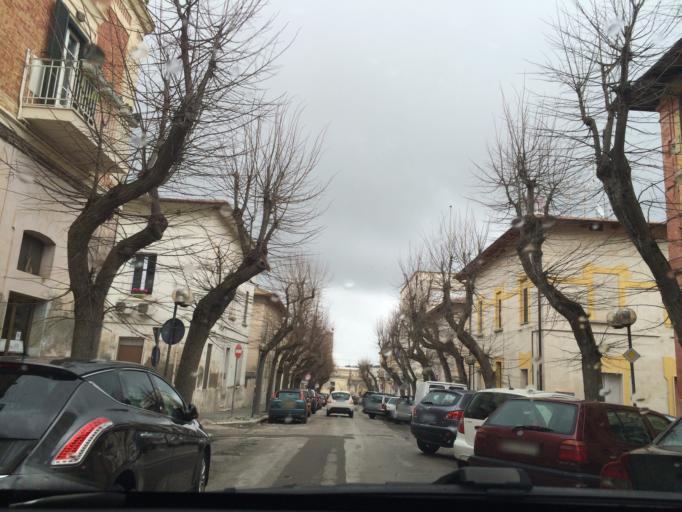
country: IT
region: Basilicate
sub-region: Provincia di Matera
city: Matera
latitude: 40.6710
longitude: 16.6066
